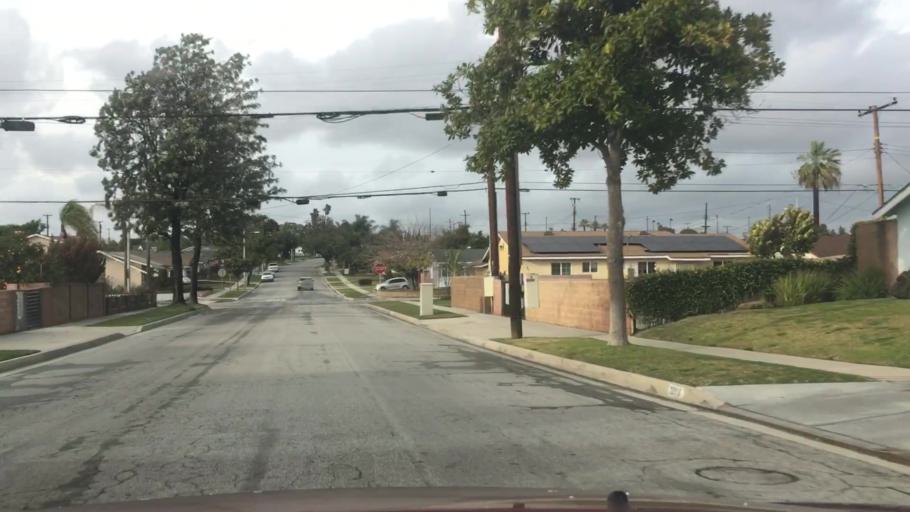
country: US
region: California
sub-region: Los Angeles County
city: La Mirada
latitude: 33.9135
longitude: -118.0236
